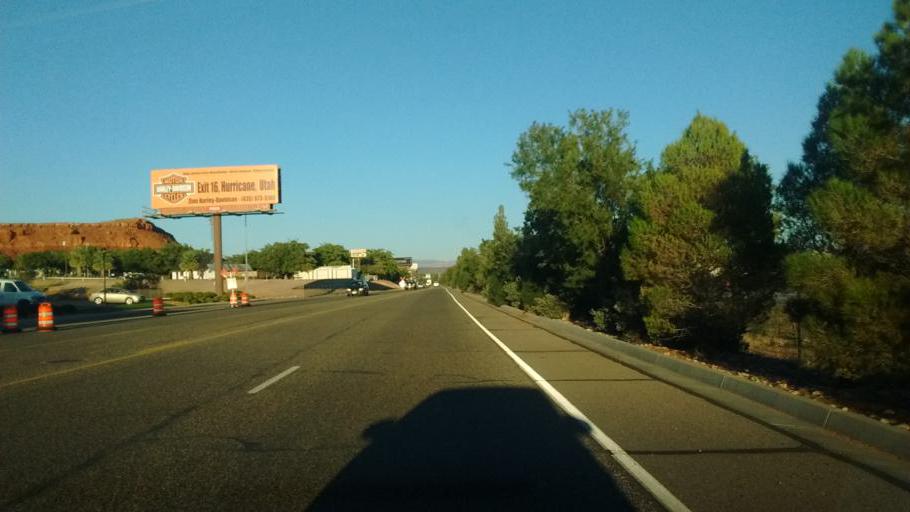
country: US
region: Utah
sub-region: Washington County
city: Washington
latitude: 37.1215
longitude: -113.5403
